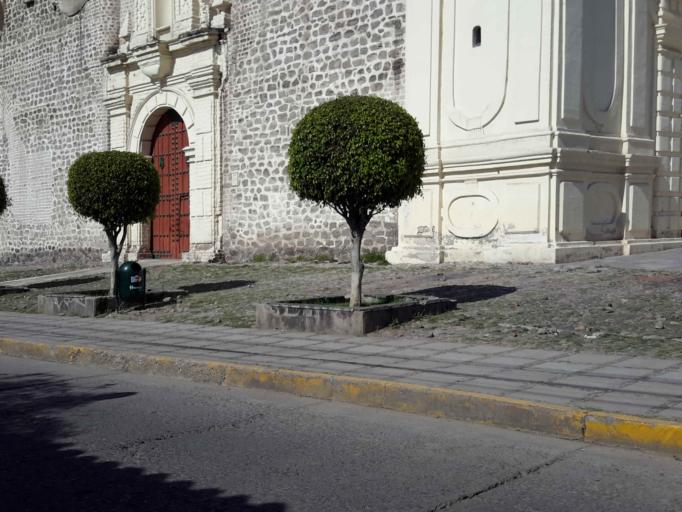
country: PE
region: Ayacucho
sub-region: Provincia de Huamanga
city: Ayacucho
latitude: -13.1676
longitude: -74.2276
